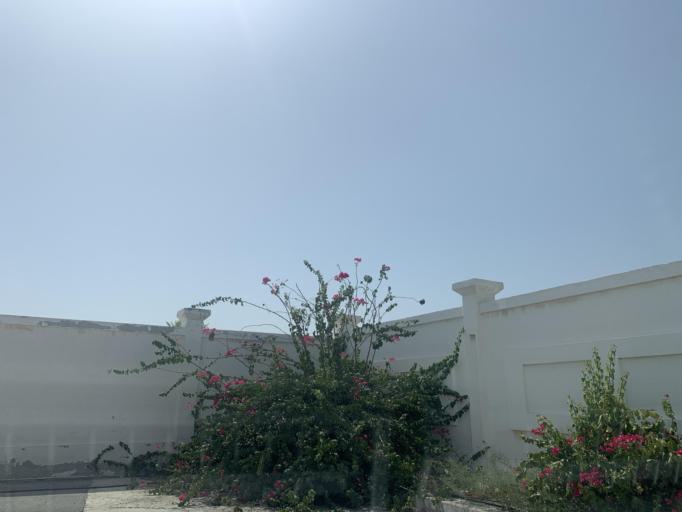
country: BH
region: Central Governorate
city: Madinat Hamad
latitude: 26.1473
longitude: 50.4927
